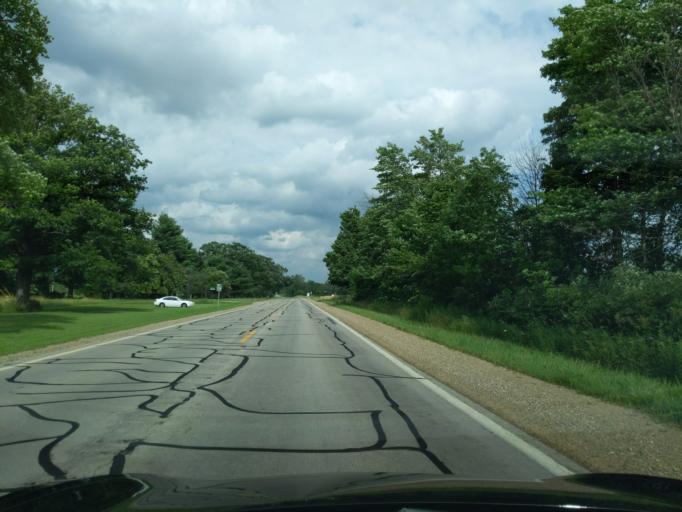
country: US
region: Michigan
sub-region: Eaton County
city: Eaton Rapids
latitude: 42.4148
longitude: -84.6247
